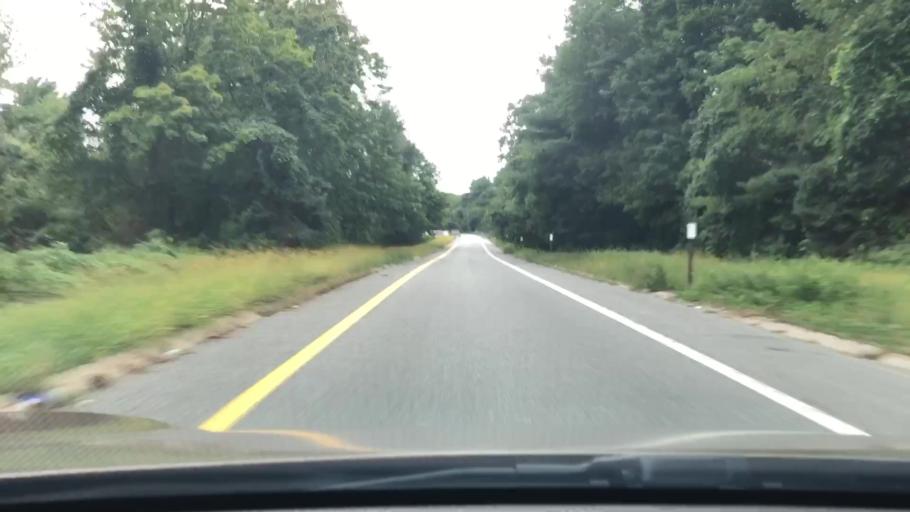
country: US
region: New York
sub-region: Westchester County
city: Briarcliff Manor
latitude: 41.1435
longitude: -73.8167
